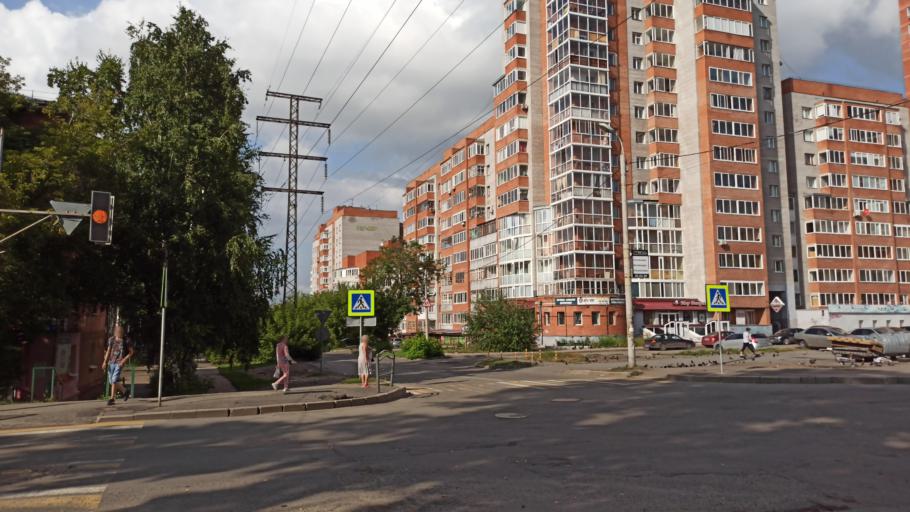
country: RU
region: Tomsk
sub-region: Tomskiy Rayon
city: Tomsk
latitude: 56.4821
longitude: 84.9999
